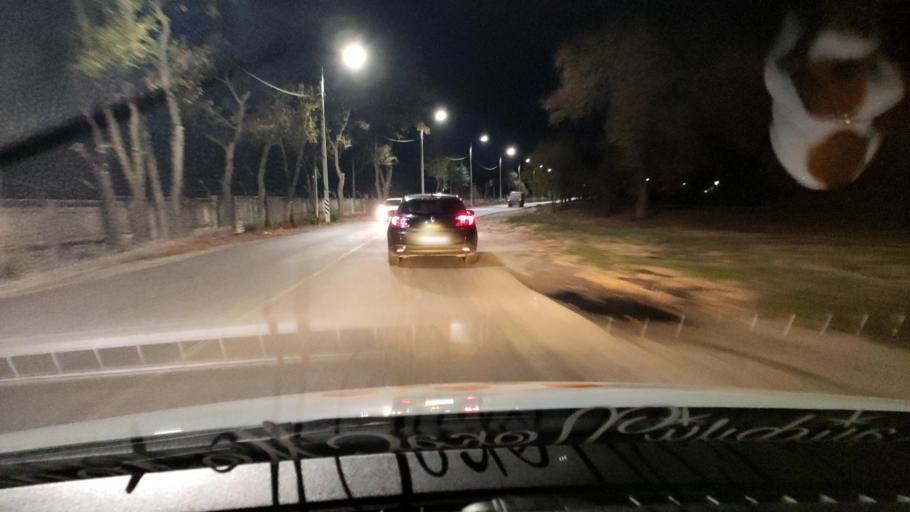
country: RU
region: Voronezj
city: Semiluki
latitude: 51.6798
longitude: 39.0294
